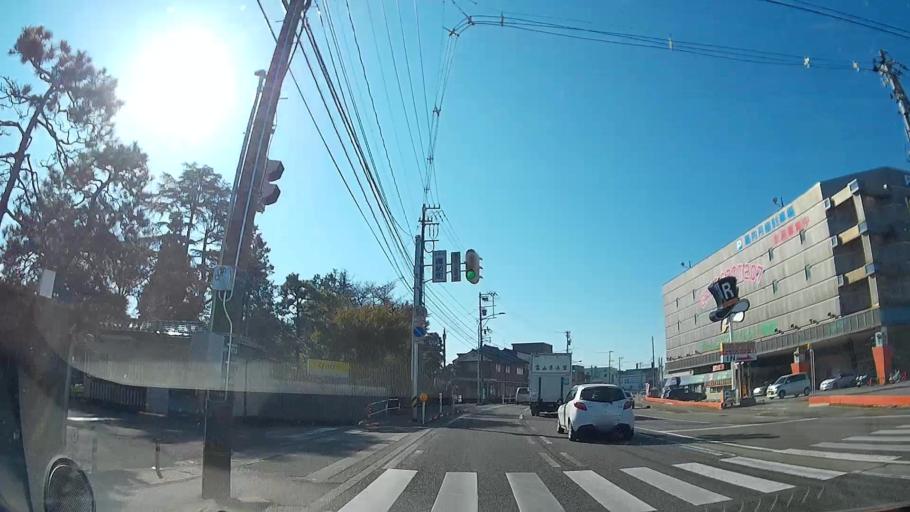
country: JP
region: Toyama
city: Takaoka
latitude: 36.7328
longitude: 137.0030
